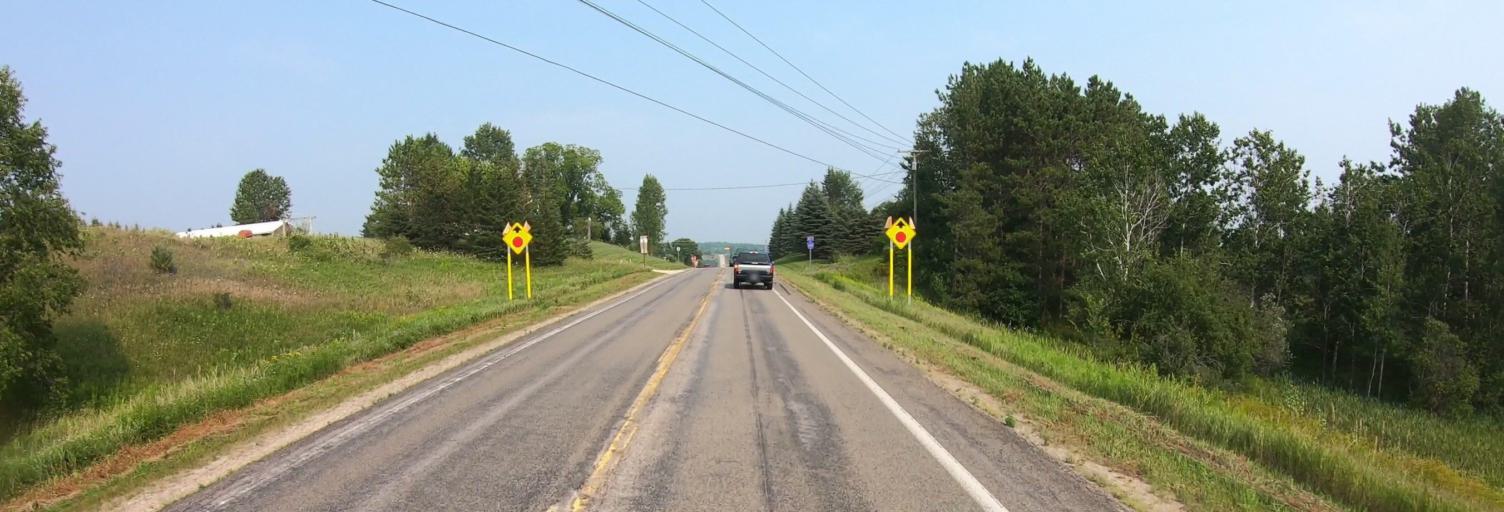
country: US
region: Michigan
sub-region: Charlevoix County
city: Charlevoix
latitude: 45.1841
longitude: -85.2662
